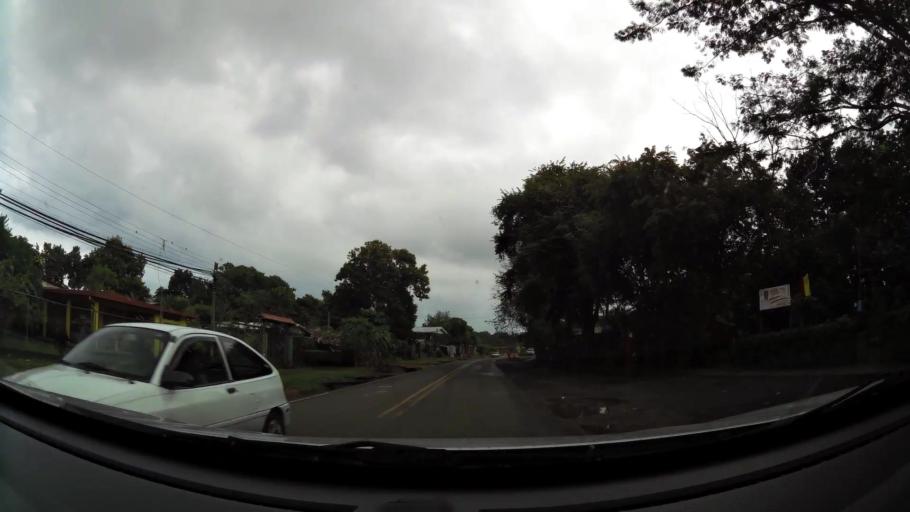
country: CR
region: Puntarenas
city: Esparza
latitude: 9.9952
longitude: -84.6459
